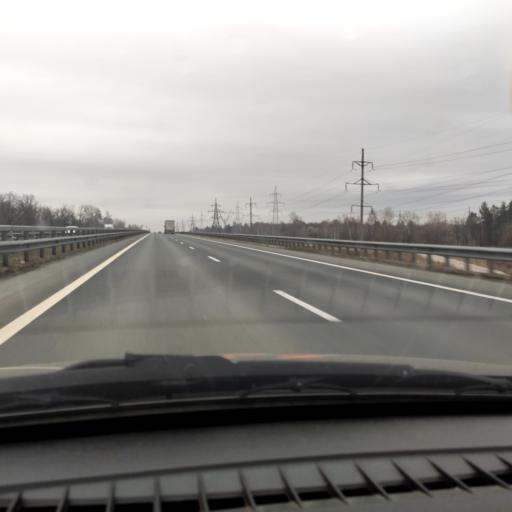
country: RU
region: Samara
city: Pribrezhnyy
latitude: 53.5176
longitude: 49.8287
